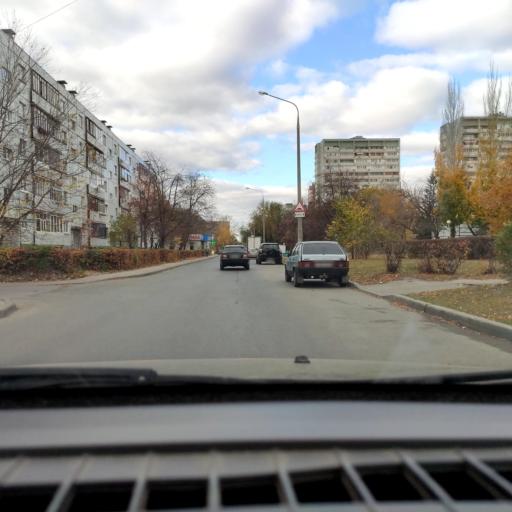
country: RU
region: Samara
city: Tol'yatti
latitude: 53.5247
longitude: 49.3091
